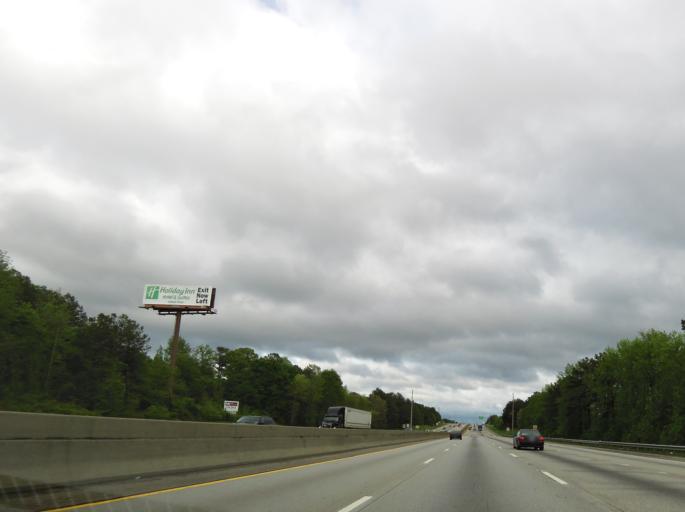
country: US
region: Georgia
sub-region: Henry County
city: Stockbridge
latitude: 33.5510
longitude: -84.2893
